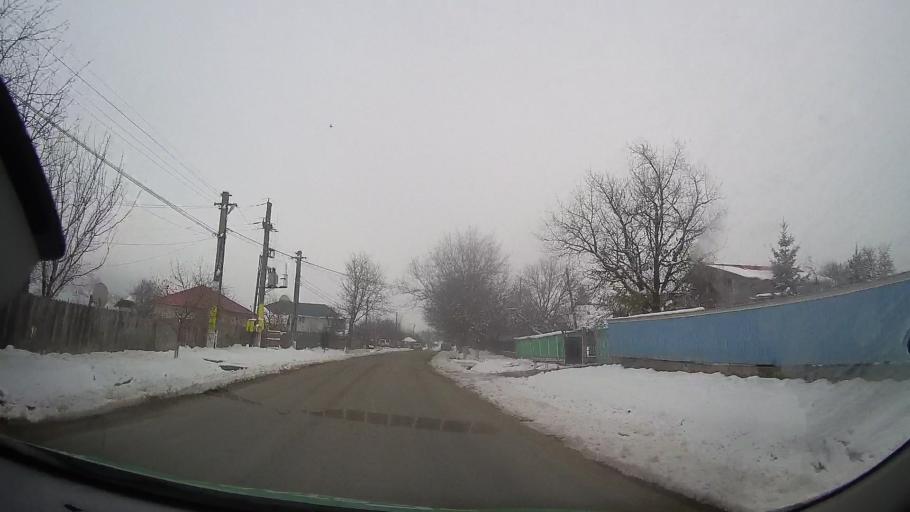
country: RO
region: Bacau
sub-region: Comuna Vultureni
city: Vultureni
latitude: 46.4027
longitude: 27.2732
